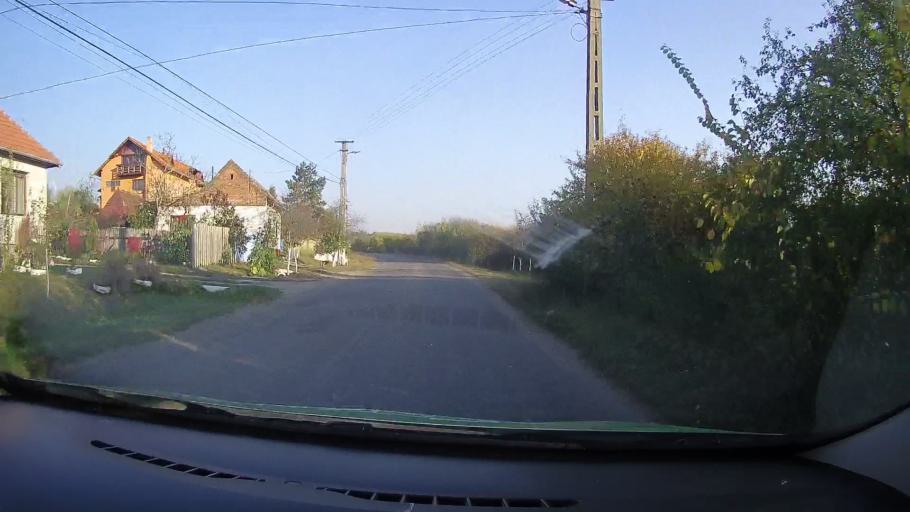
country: RO
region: Arad
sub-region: Comuna Silindia
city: Silindia
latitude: 46.3372
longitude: 21.9242
